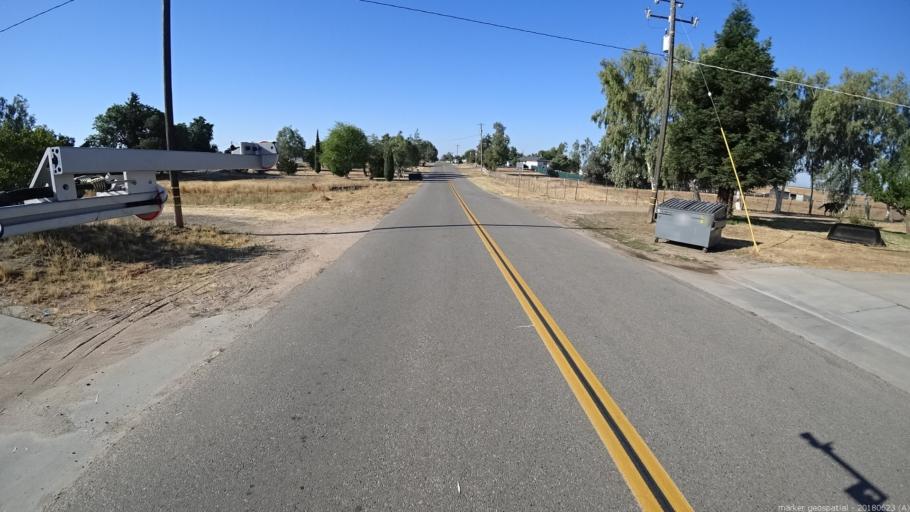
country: US
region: California
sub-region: Madera County
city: Bonadelle Ranchos-Madera Ranchos
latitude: 36.9664
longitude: -119.8015
